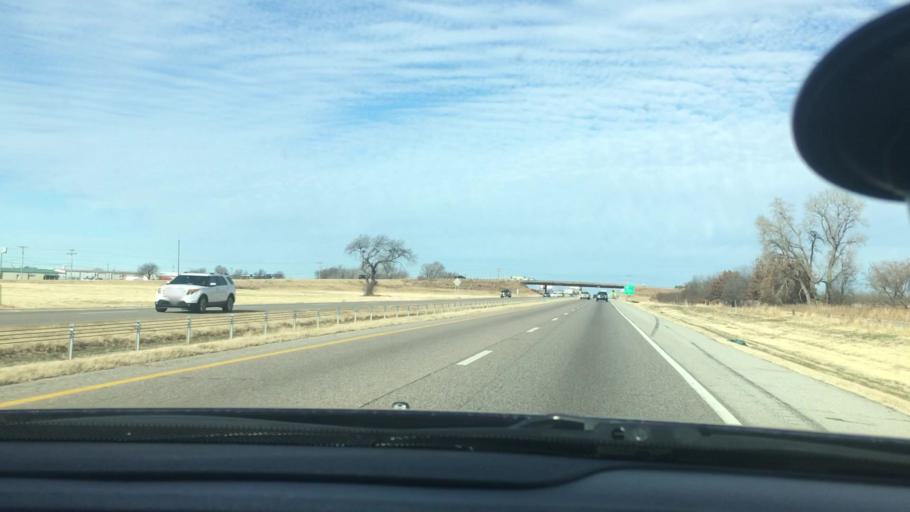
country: US
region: Oklahoma
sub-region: McClain County
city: Goldsby
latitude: 35.1501
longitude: -97.4738
